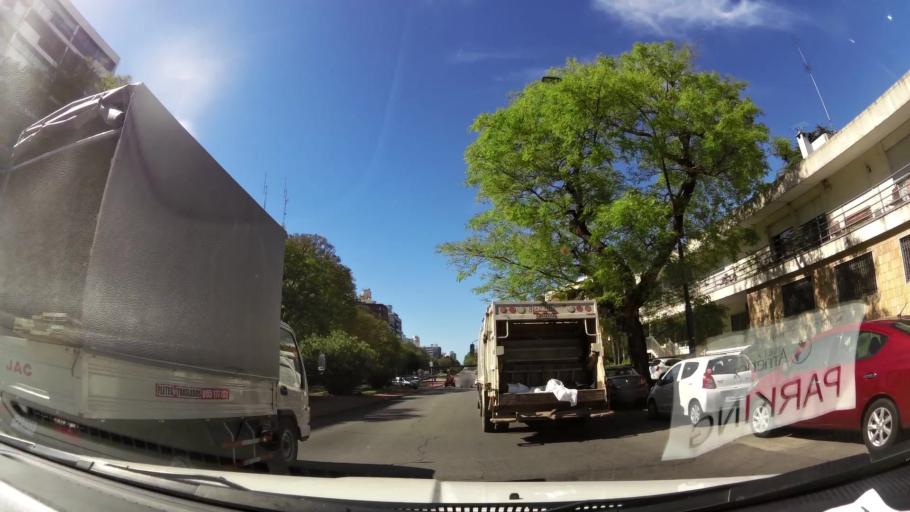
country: UY
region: Montevideo
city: Montevideo
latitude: -34.9119
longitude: -56.1632
